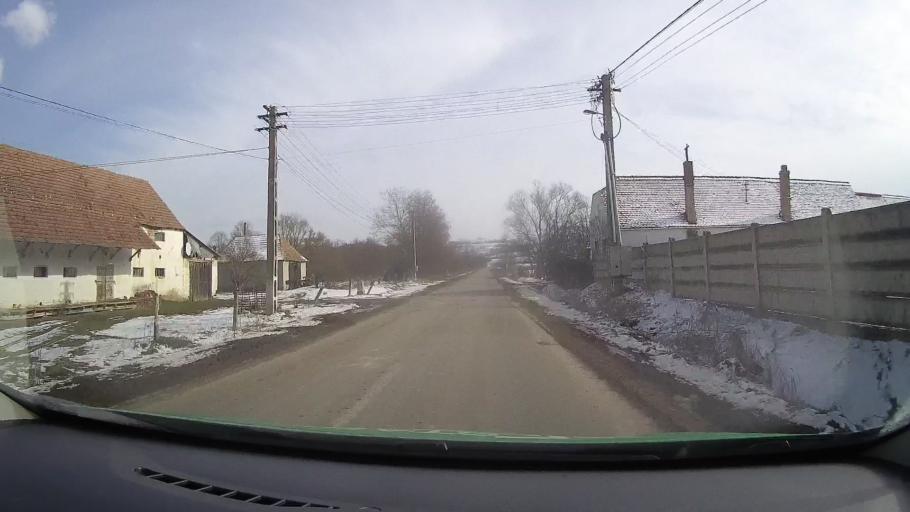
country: RO
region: Mures
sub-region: Comuna Apold
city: Apold
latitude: 46.1211
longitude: 24.8217
